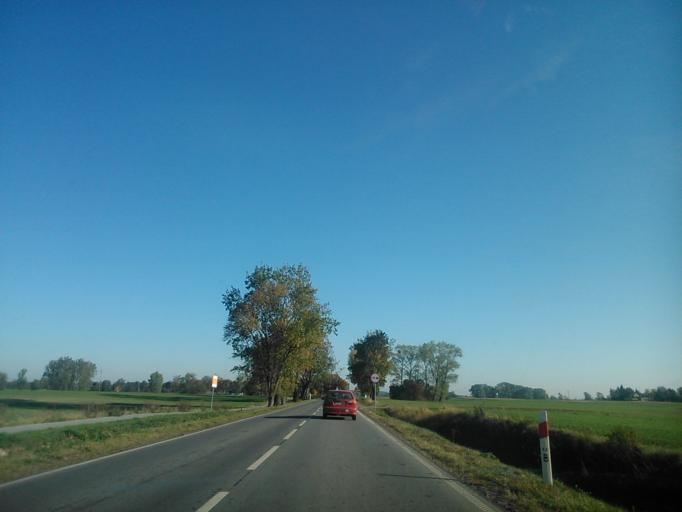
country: PL
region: Kujawsko-Pomorskie
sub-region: Powiat wabrzeski
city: Debowa Laka
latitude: 53.2275
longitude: 19.0257
